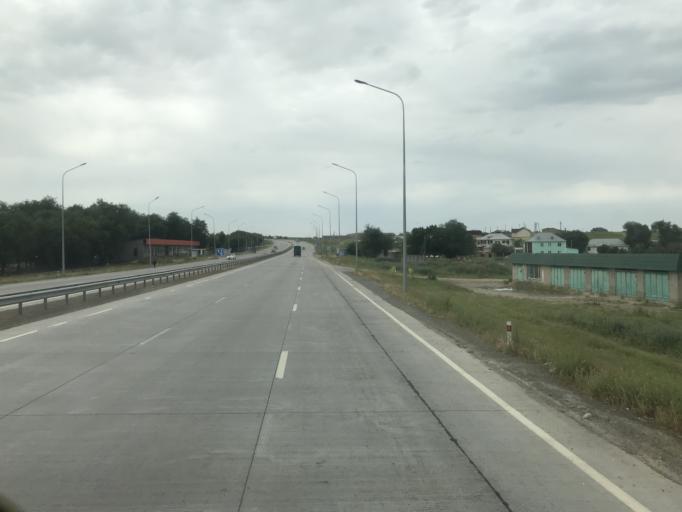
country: KZ
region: Ongtustik Qazaqstan
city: Shymkent
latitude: 42.2119
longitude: 69.5199
